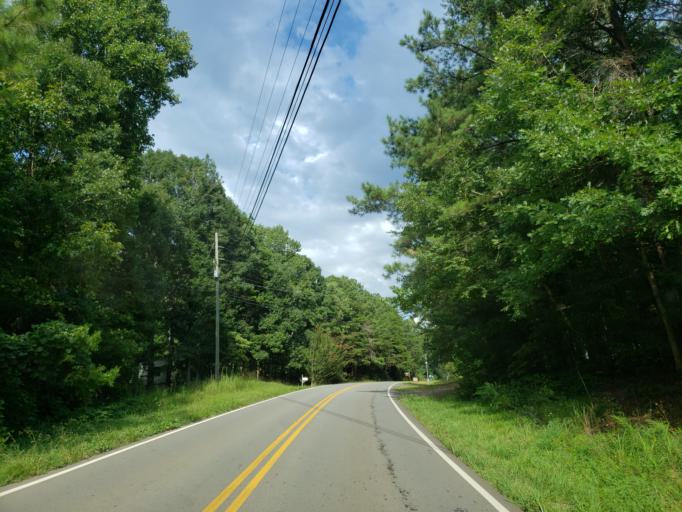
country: US
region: Georgia
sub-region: Pickens County
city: Jasper
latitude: 34.4102
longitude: -84.4897
